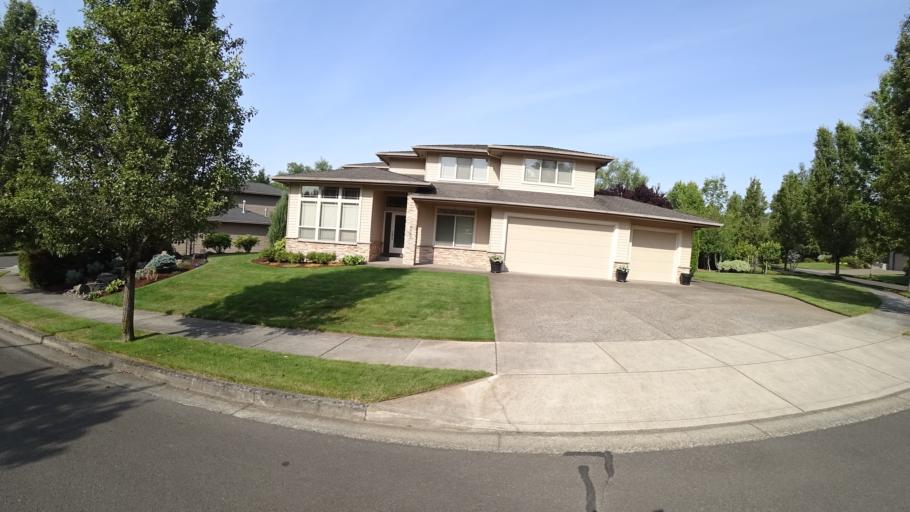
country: US
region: Oregon
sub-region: Clackamas County
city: Happy Valley
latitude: 45.4551
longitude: -122.5150
